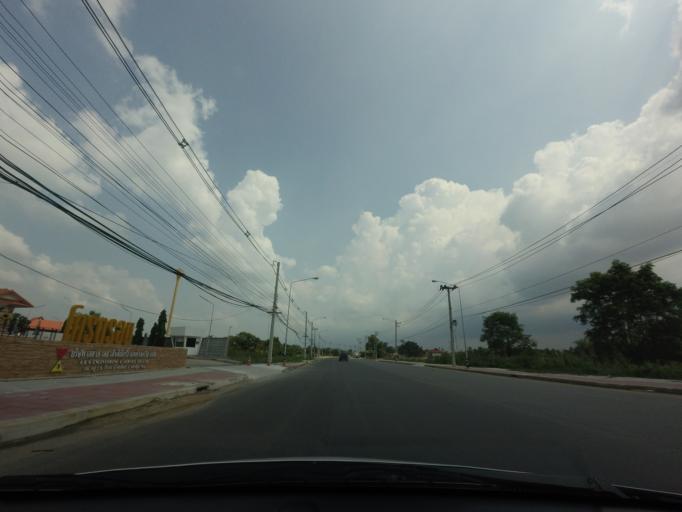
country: TH
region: Nakhon Pathom
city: Nakhon Chai Si
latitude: 13.8042
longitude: 100.2137
